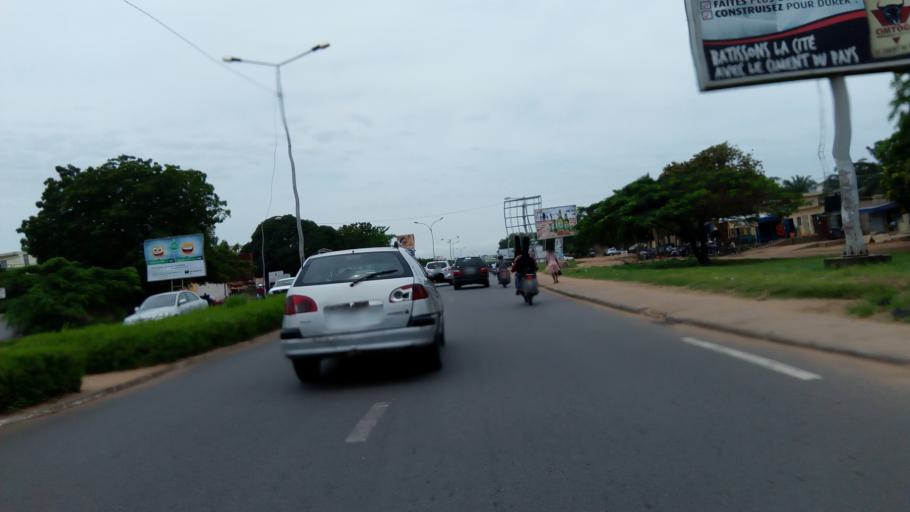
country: TG
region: Maritime
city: Lome
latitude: 6.1606
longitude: 1.2249
